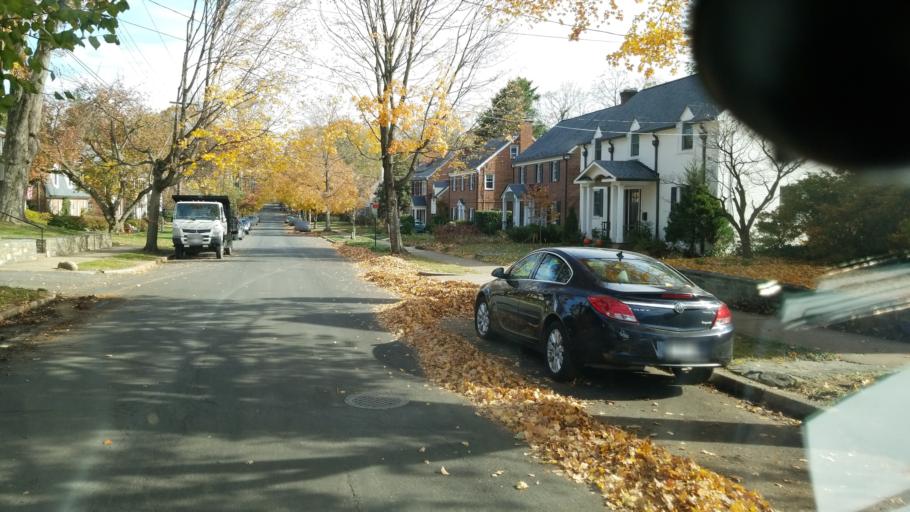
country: US
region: Maryland
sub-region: Montgomery County
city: Friendship Village
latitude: 38.9479
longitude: -77.0965
